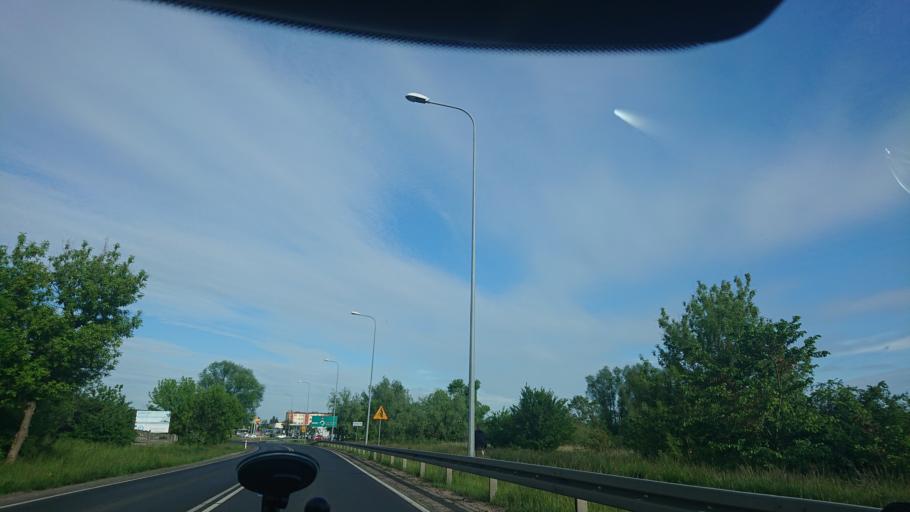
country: PL
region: Greater Poland Voivodeship
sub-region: Powiat gnieznienski
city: Gniezno
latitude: 52.5146
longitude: 17.5903
